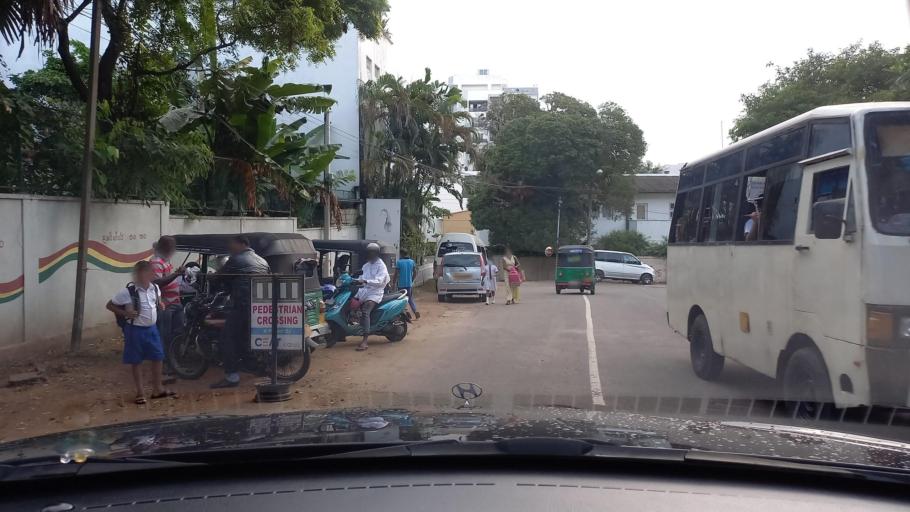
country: LK
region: Western
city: Pita Kotte
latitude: 6.8799
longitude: 79.8680
